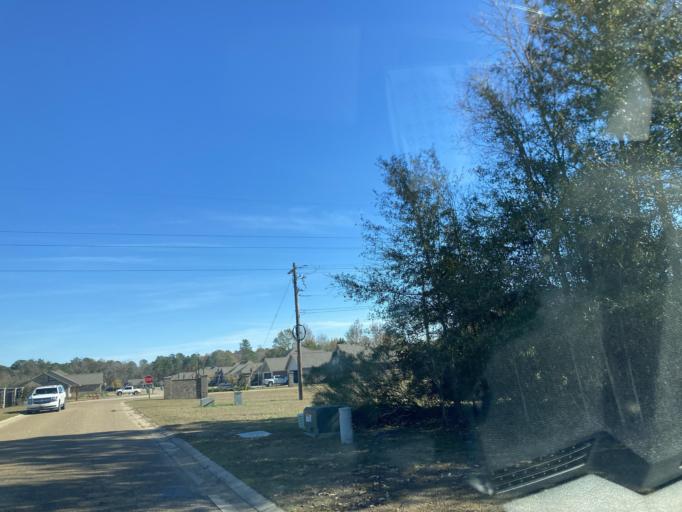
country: US
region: Mississippi
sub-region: Forrest County
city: Petal
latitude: 31.3582
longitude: -89.1972
